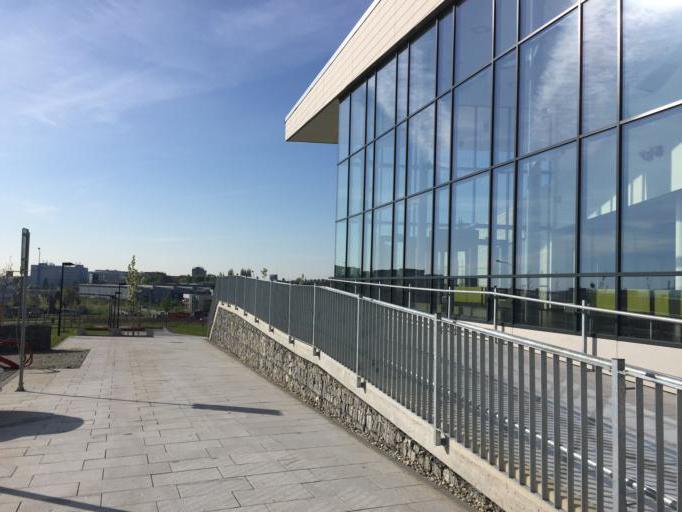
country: CZ
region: South Moravian
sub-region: Mesto Brno
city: Mokra Hora
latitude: 49.2336
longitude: 16.5747
